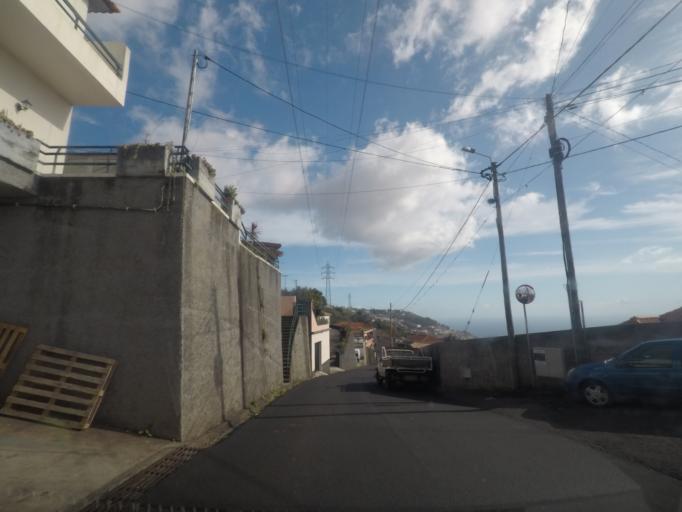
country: PT
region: Madeira
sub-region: Funchal
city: Nossa Senhora do Monte
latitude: 32.6813
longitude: -16.8999
